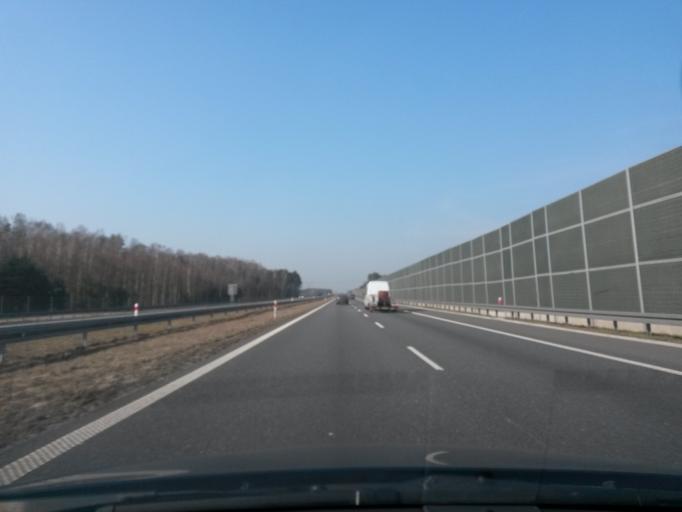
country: PL
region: Lodz Voivodeship
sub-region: powiat Lowicki
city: Nieborow
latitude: 52.0497
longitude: 20.0928
